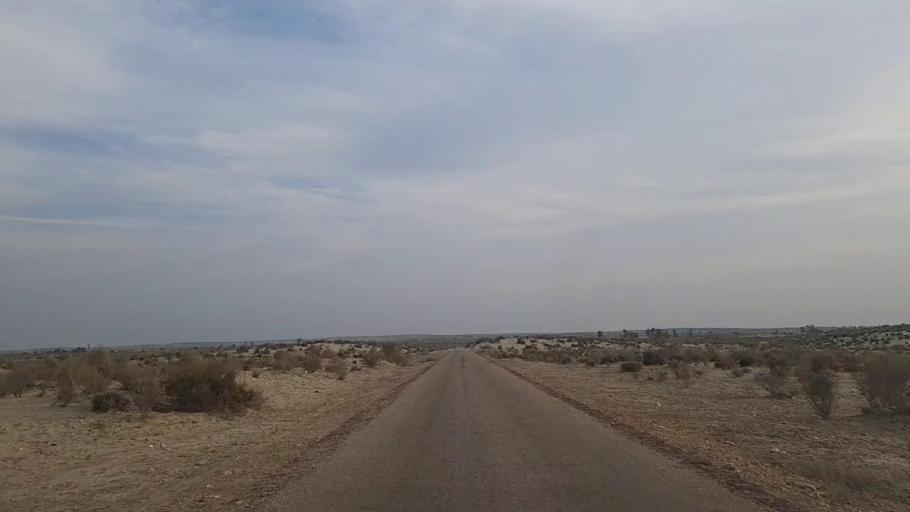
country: PK
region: Sindh
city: Daur
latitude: 26.5015
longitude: 68.5201
